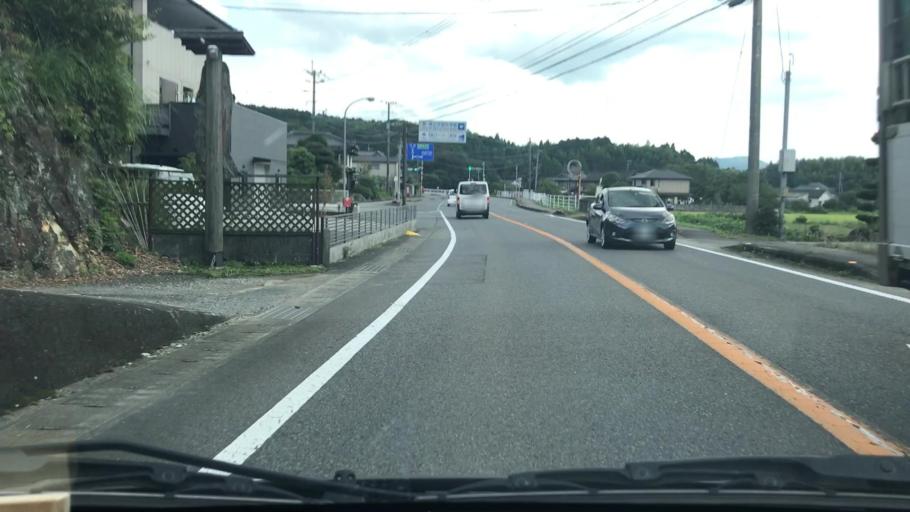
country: JP
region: Saga Prefecture
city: Takeocho-takeo
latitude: 33.2271
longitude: 130.0235
